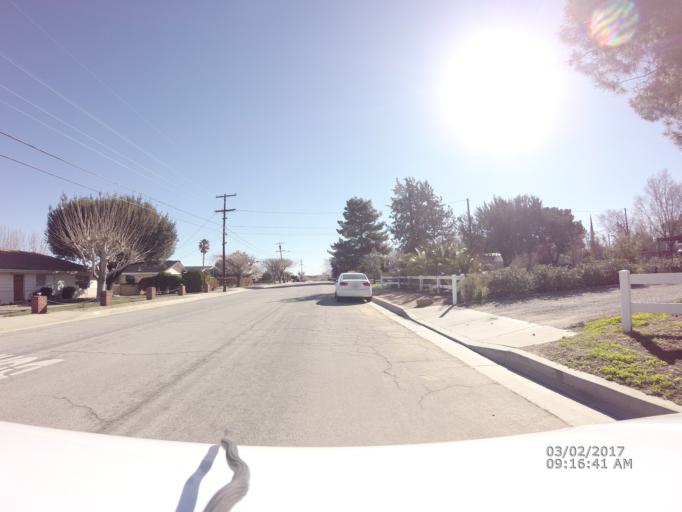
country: US
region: California
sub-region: Los Angeles County
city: Quartz Hill
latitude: 34.6345
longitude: -118.2119
